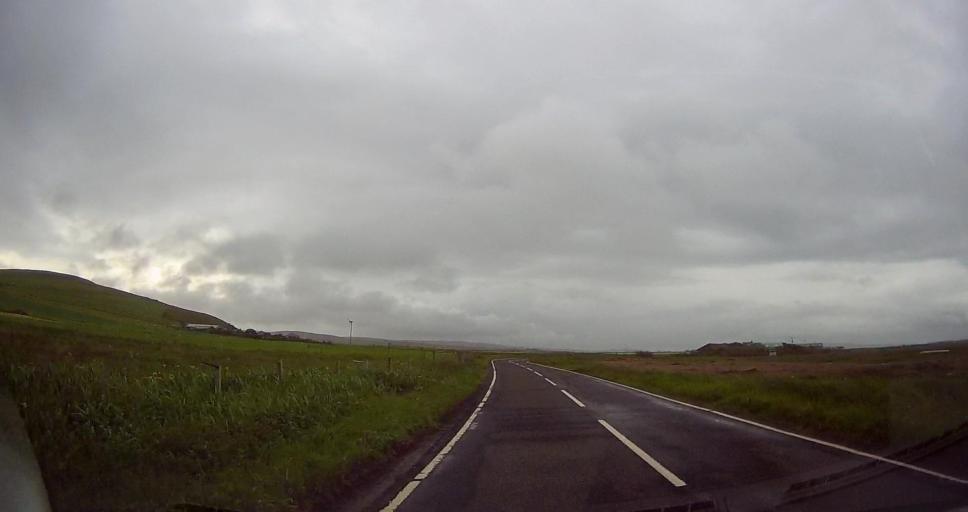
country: GB
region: Scotland
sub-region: Orkney Islands
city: Stromness
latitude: 59.0884
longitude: -3.2588
